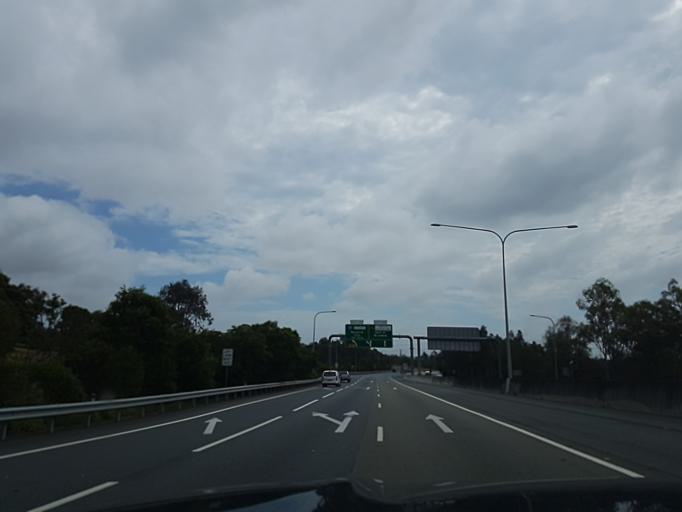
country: AU
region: Queensland
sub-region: Brisbane
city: Cannon Hill
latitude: -27.4552
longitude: 153.1110
